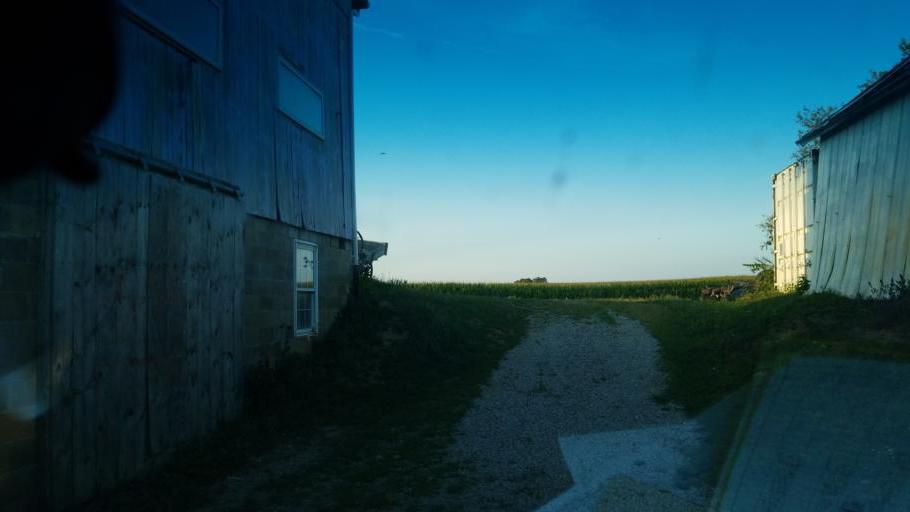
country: US
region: Ohio
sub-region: Knox County
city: Fredericktown
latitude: 40.4974
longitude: -82.6136
